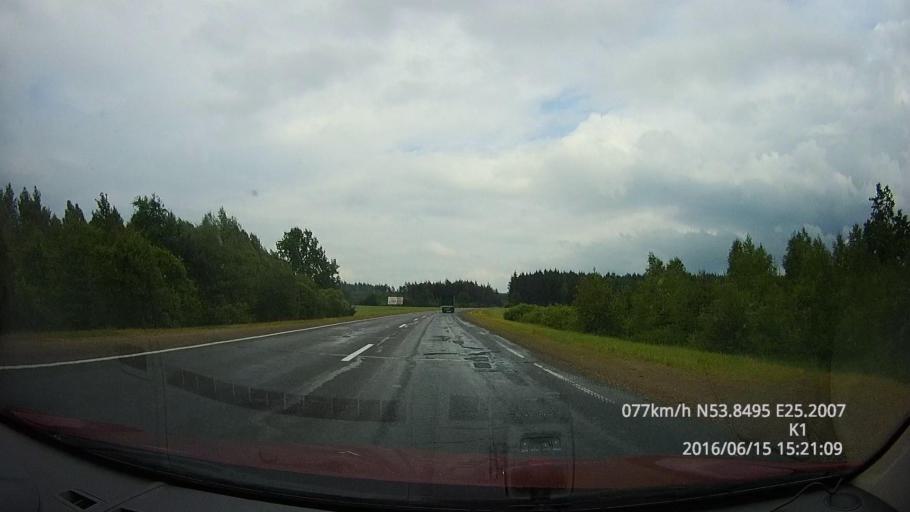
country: BY
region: Grodnenskaya
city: Lida
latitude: 53.8496
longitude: 25.2018
